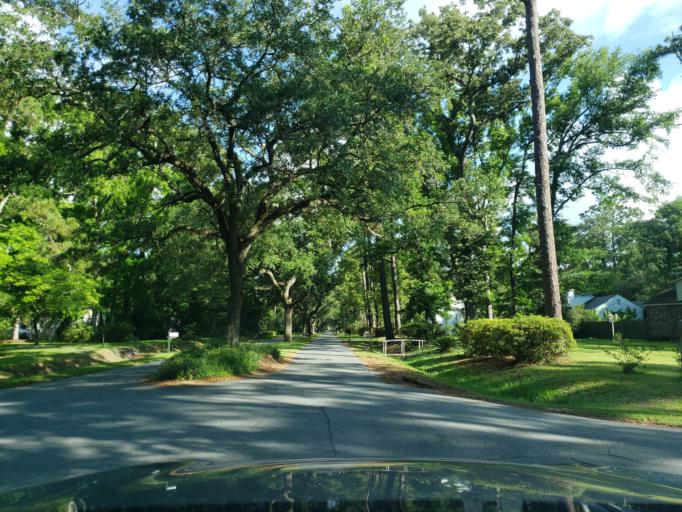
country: US
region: Georgia
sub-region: Chatham County
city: Isle of Hope
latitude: 31.9754
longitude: -81.0594
